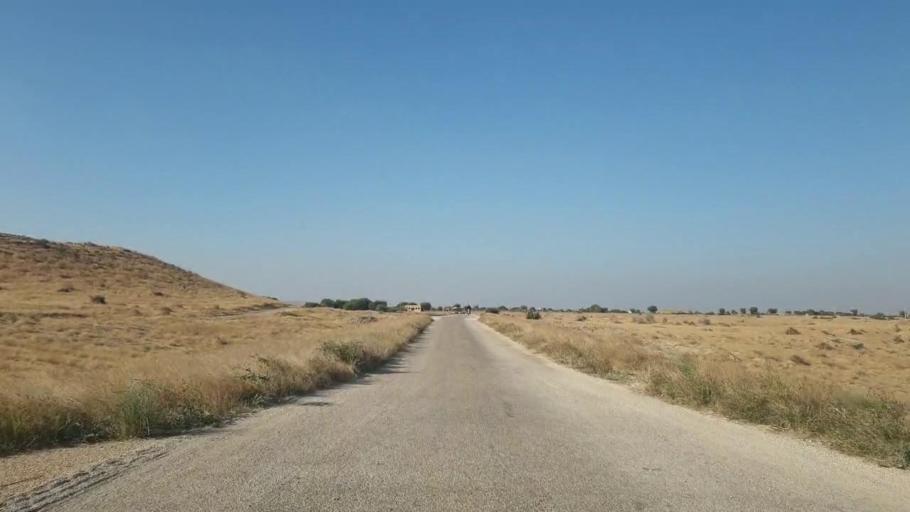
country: PK
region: Sindh
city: Malir Cantonment
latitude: 25.4173
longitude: 67.4639
